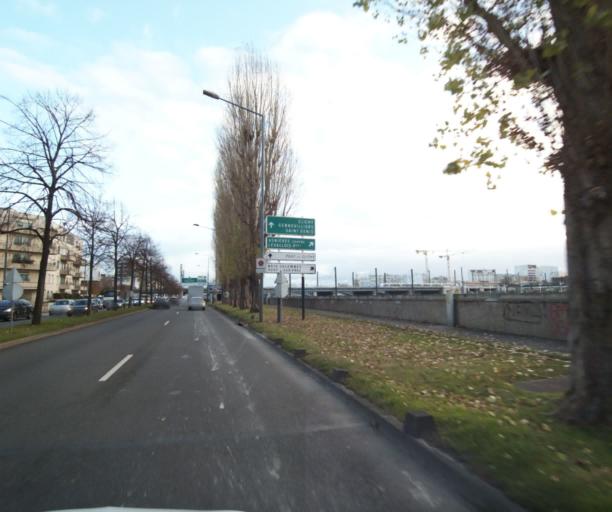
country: FR
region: Ile-de-France
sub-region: Departement des Hauts-de-Seine
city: Levallois-Perret
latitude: 48.9030
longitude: 2.2838
